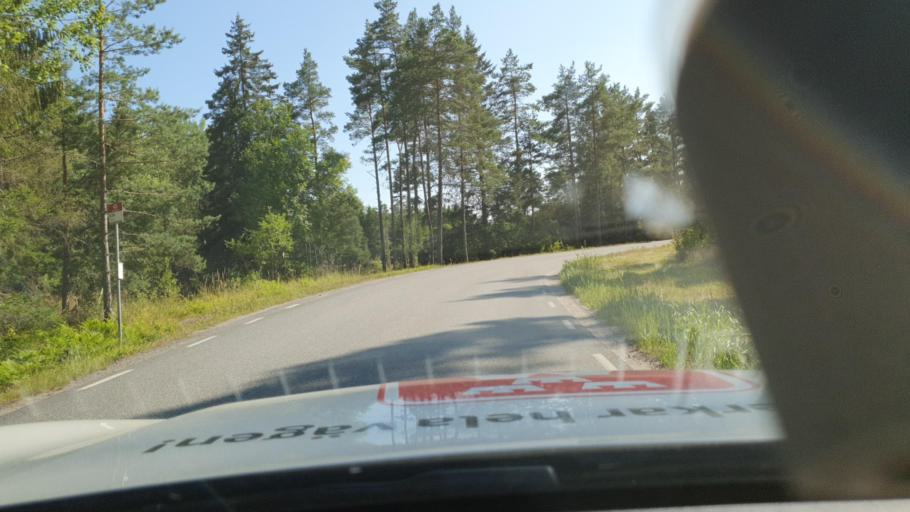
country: SE
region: Stockholm
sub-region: Norrtalje Kommun
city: Bjorko
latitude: 59.8130
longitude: 18.9408
